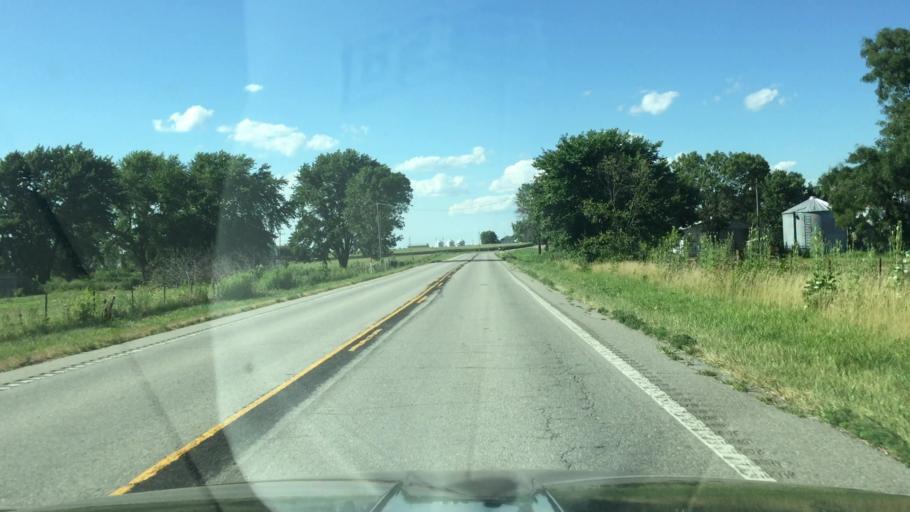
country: US
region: Missouri
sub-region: Moniteau County
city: Tipton
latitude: 38.6055
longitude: -92.7899
